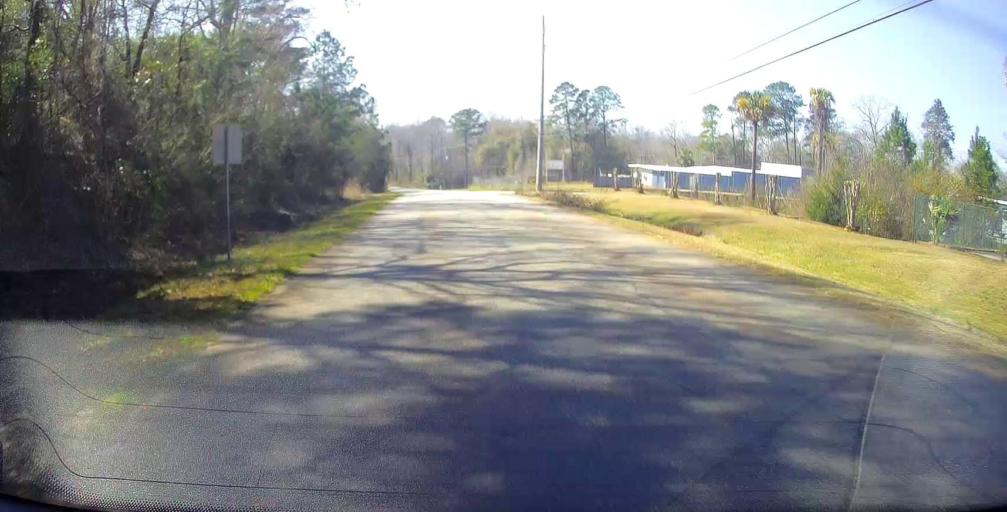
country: US
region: Georgia
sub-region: Houston County
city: Perry
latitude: 32.4658
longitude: -83.7581
